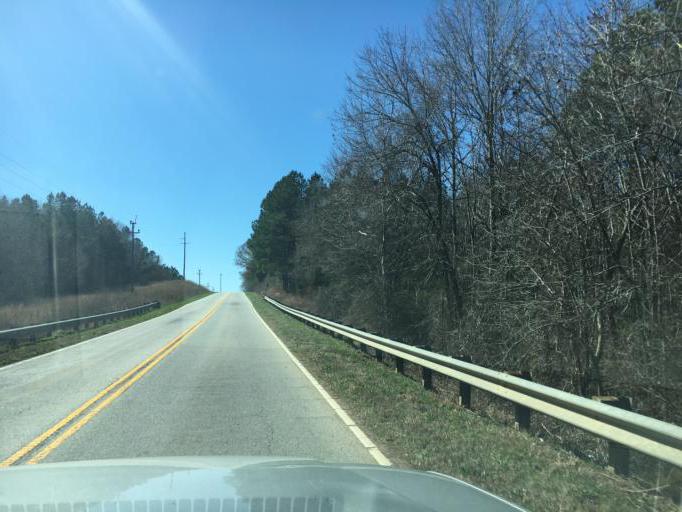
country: US
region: South Carolina
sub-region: Greenwood County
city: Ninety Six
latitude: 34.1937
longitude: -81.8457
